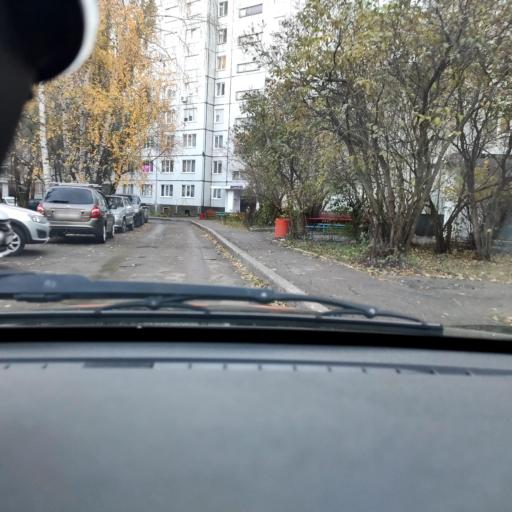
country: RU
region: Samara
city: Tol'yatti
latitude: 53.5077
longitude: 49.4406
